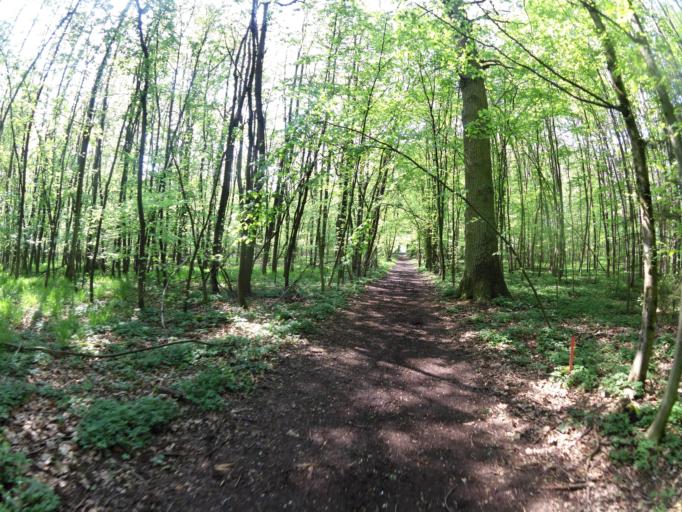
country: DE
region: Bavaria
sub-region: Regierungsbezirk Unterfranken
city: Sommerhausen
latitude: 49.7068
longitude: 10.0559
